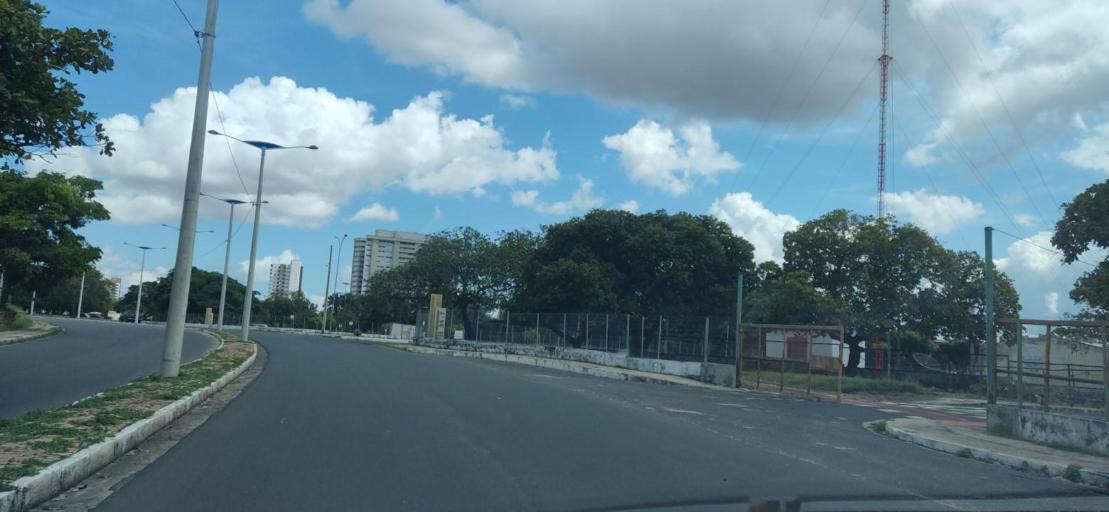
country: BR
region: Piaui
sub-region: Teresina
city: Teresina
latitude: -5.0591
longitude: -42.7953
